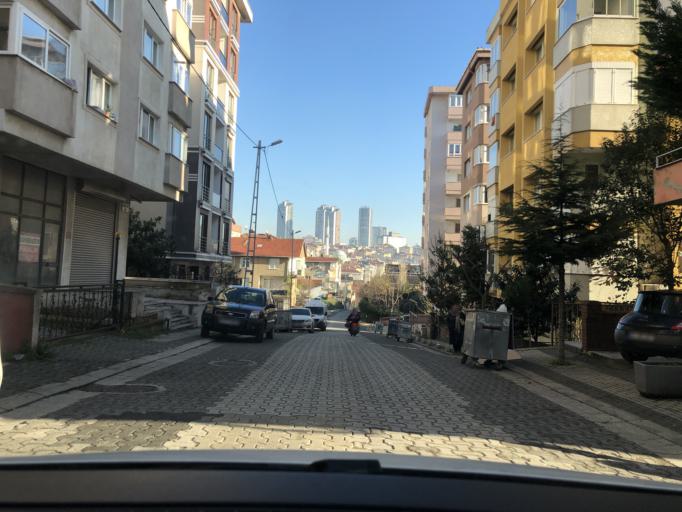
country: TR
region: Istanbul
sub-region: Atasehir
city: Atasehir
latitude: 40.9737
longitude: 29.1228
